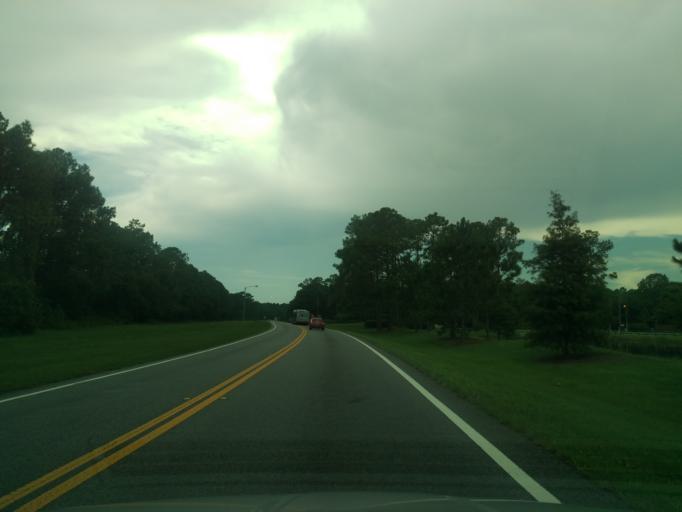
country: US
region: Florida
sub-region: Osceola County
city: Celebration
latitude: 28.3946
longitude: -81.5521
